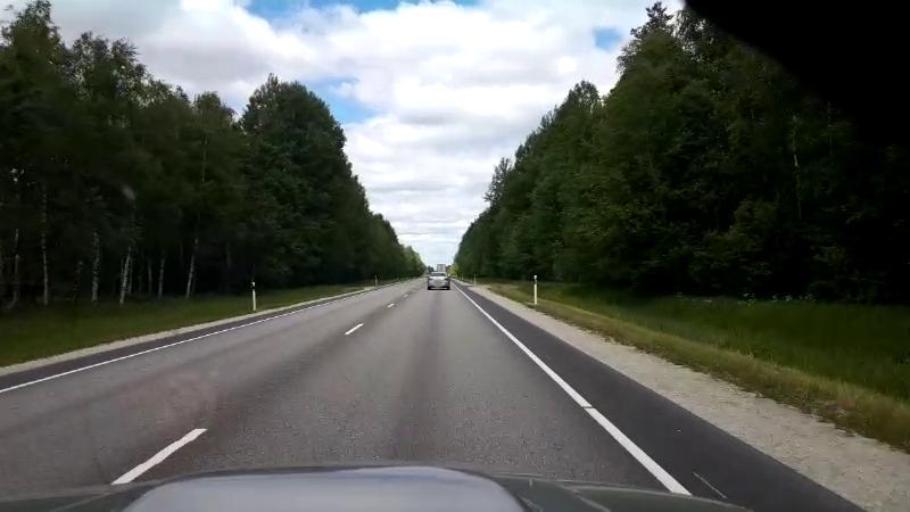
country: EE
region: Paernumaa
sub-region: Halinga vald
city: Parnu-Jaagupi
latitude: 58.7300
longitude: 24.4236
